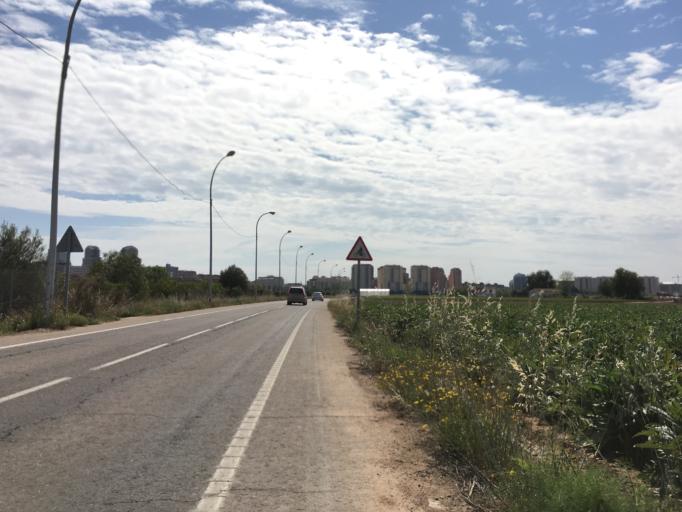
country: ES
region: Valencia
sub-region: Provincia de Valencia
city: Mislata
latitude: 39.4902
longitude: -0.4152
